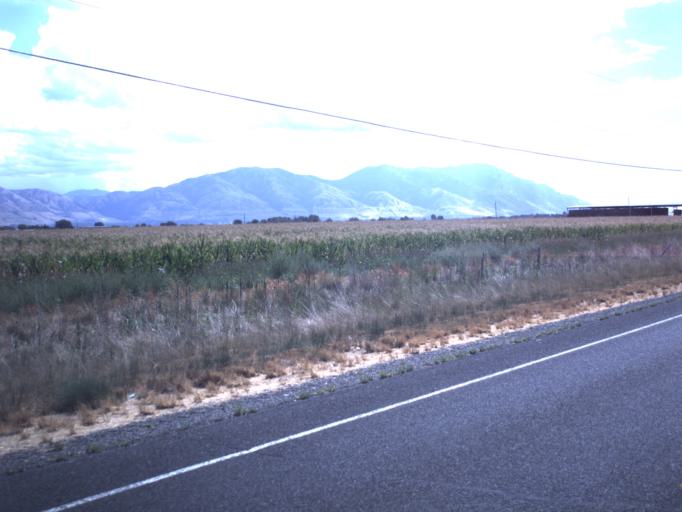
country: US
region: Utah
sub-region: Box Elder County
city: Honeyville
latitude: 41.5867
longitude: -112.1298
